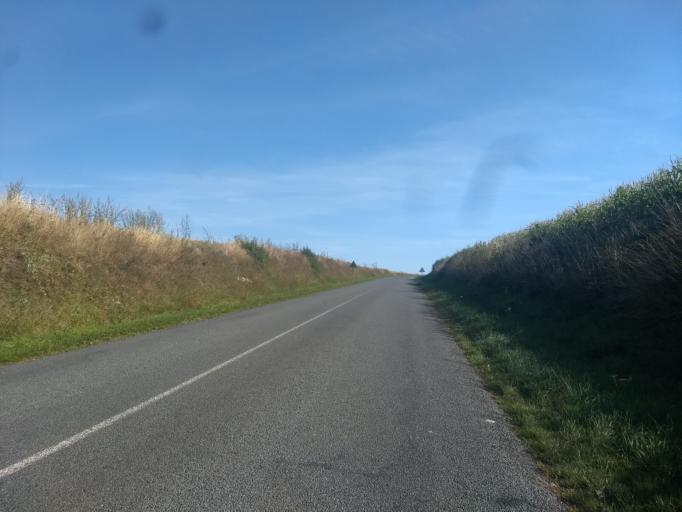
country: FR
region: Nord-Pas-de-Calais
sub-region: Departement du Pas-de-Calais
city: Roeux
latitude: 50.2871
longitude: 2.9001
